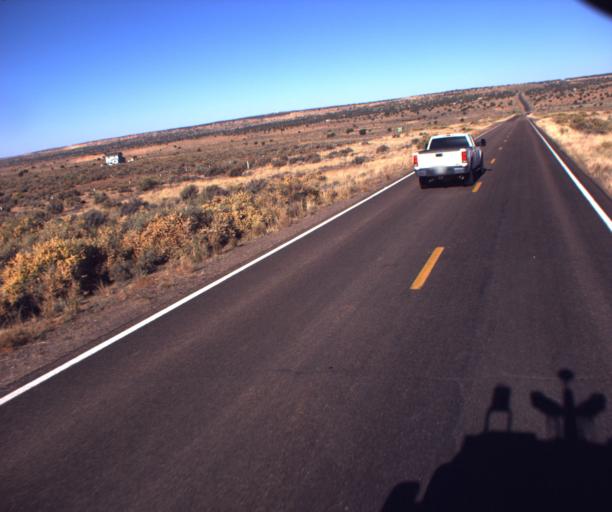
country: US
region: Arizona
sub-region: Navajo County
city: First Mesa
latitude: 35.7507
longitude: -110.1309
